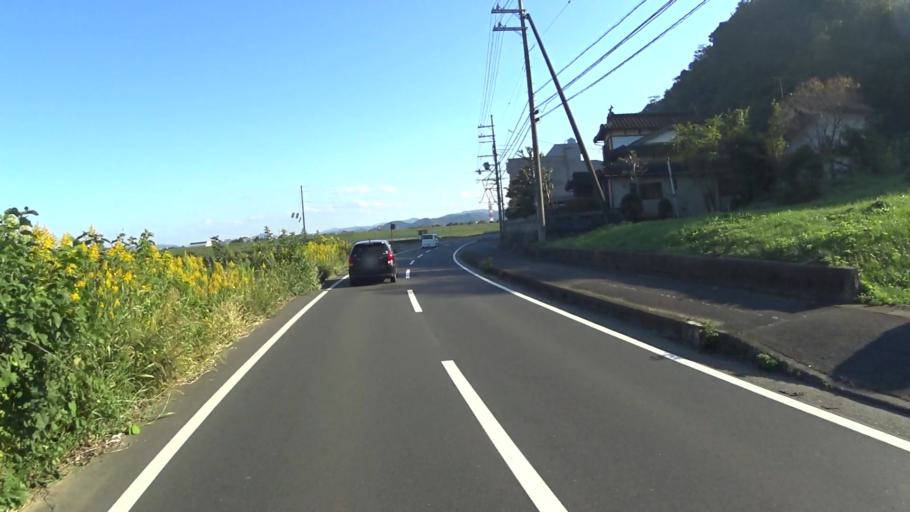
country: JP
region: Kyoto
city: Fukuchiyama
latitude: 35.3187
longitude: 135.1088
